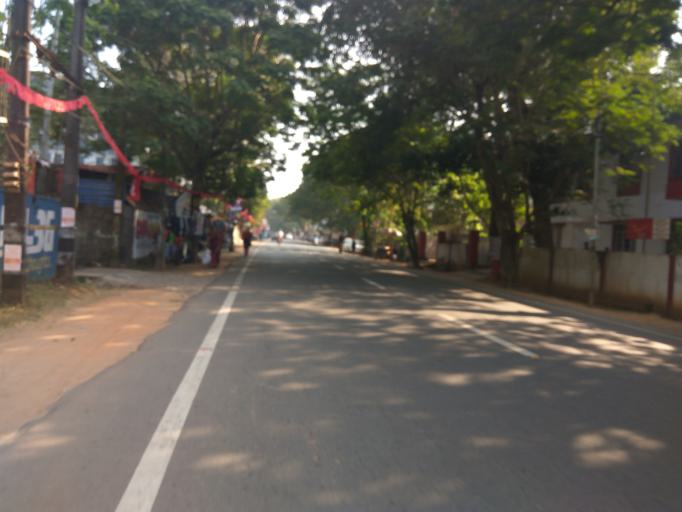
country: IN
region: Kerala
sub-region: Kozhikode
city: Kozhikode
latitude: 11.2825
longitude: 75.7699
